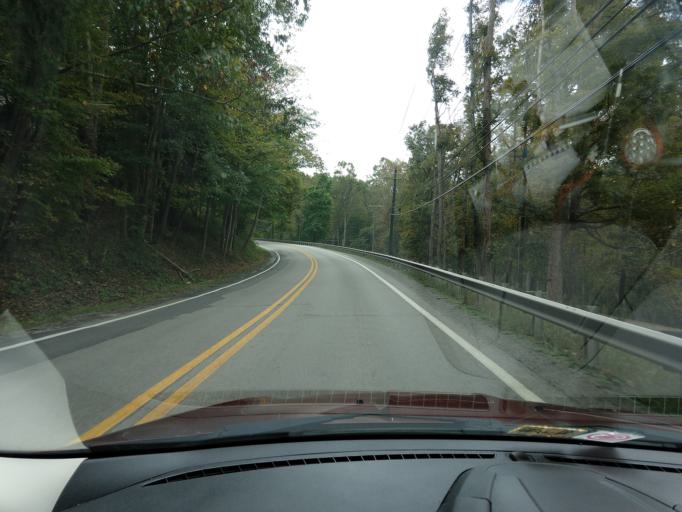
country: US
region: West Virginia
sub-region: Barbour County
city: Belington
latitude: 39.0182
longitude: -79.9392
